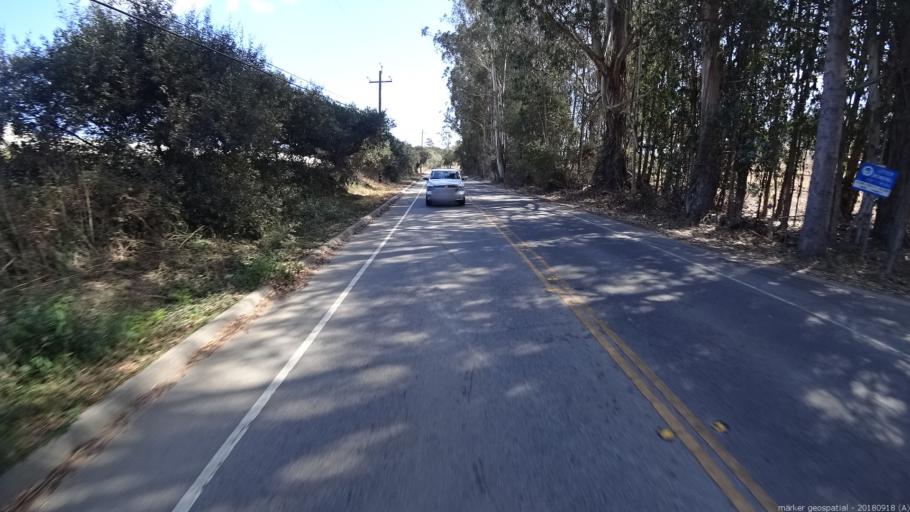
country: US
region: California
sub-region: Monterey County
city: Prunedale
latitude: 36.7759
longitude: -121.6859
